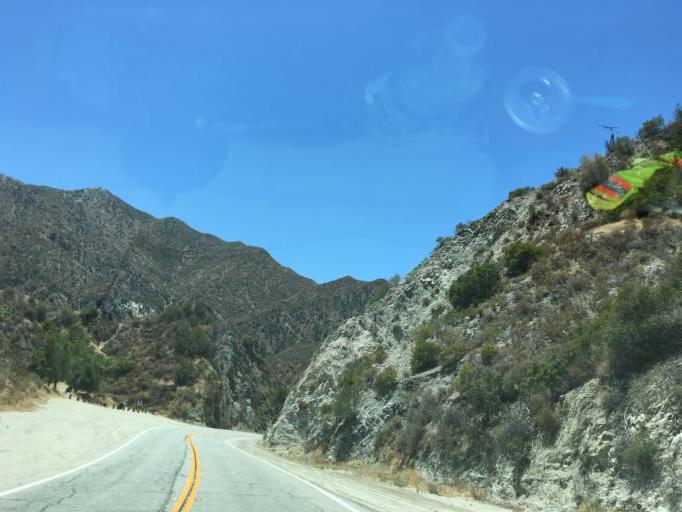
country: US
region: California
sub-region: Los Angeles County
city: La Crescenta-Montrose
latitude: 34.3042
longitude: -118.2641
